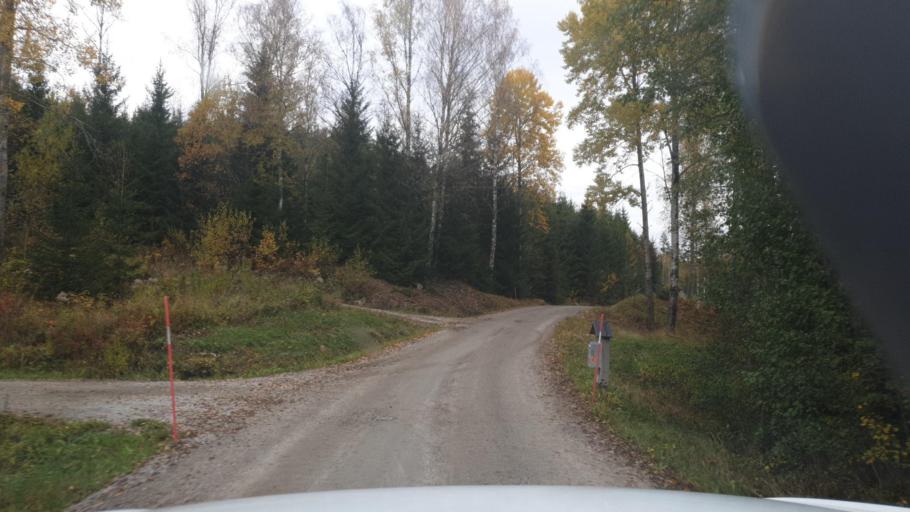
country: SE
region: Vaermland
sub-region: Arvika Kommun
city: Arvika
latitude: 59.6773
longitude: 12.7679
